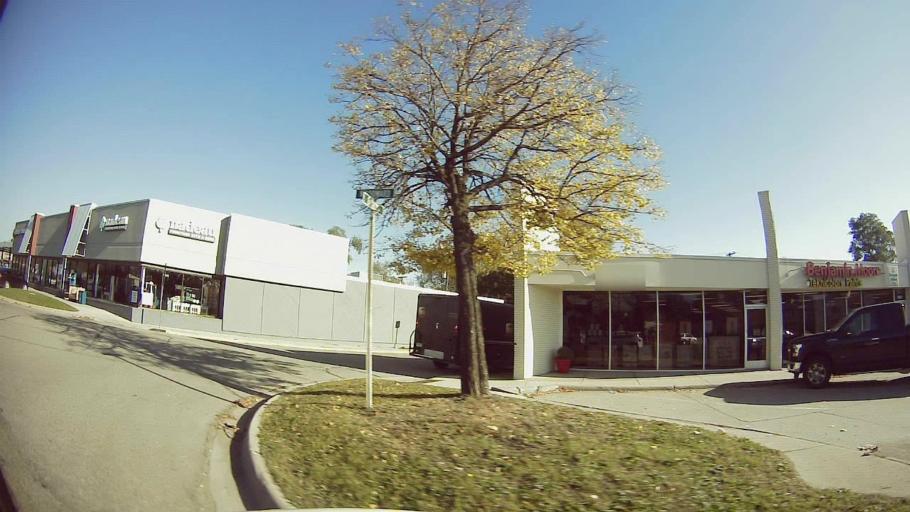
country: US
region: Michigan
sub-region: Oakland County
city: Birmingham
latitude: 42.5349
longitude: -83.2023
